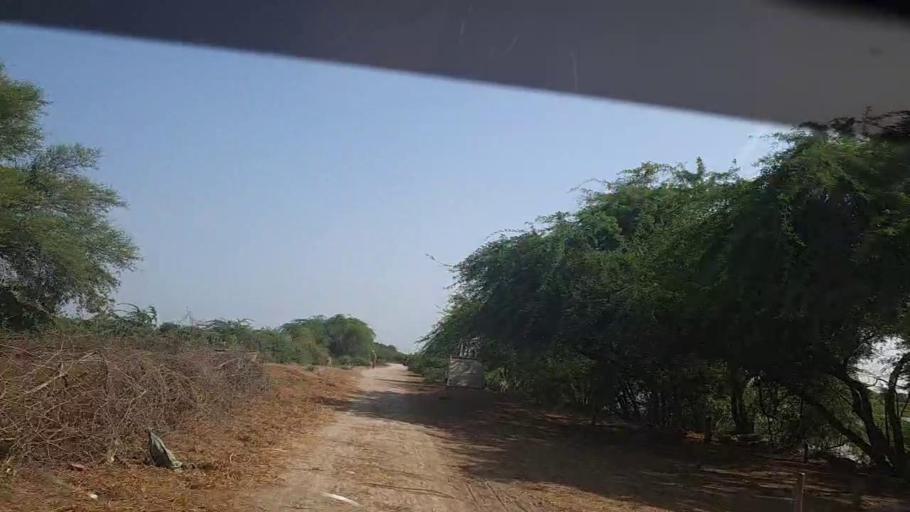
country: PK
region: Sindh
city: Rajo Khanani
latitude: 24.9650
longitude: 68.8900
